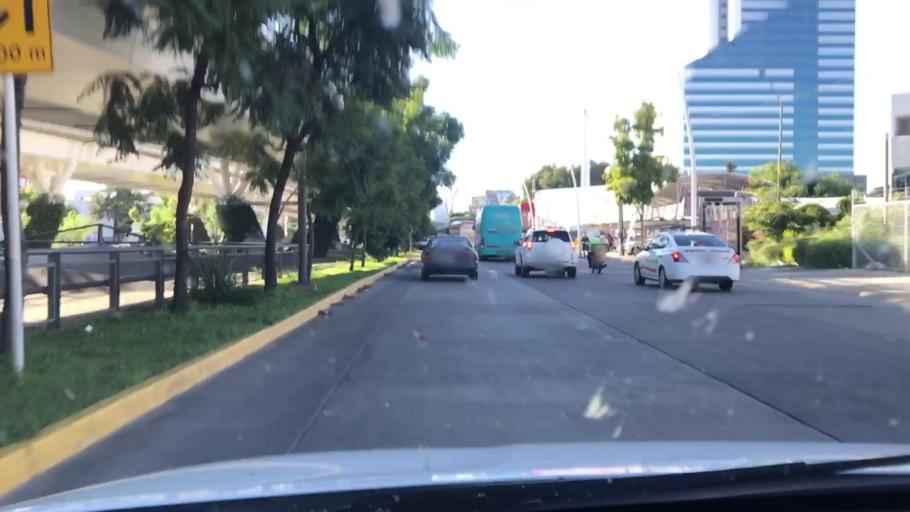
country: MX
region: Jalisco
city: Guadalajara
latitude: 20.6640
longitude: -103.3919
